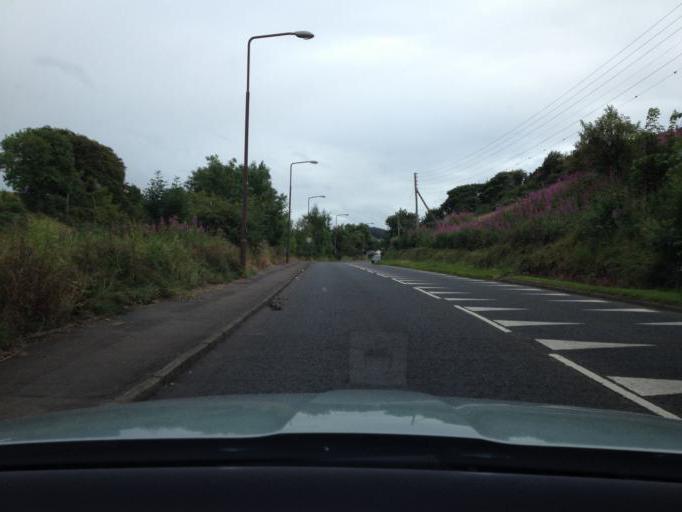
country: GB
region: Scotland
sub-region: West Lothian
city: Bathgate
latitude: 55.9327
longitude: -3.6526
